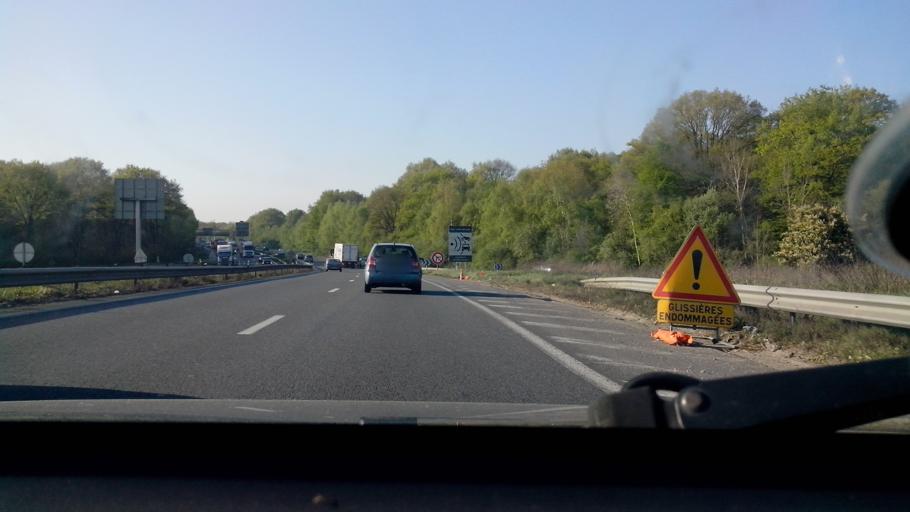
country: FR
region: Ile-de-France
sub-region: Departement de Seine-et-Marne
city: Pontault-Combault
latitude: 48.7730
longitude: 2.6117
